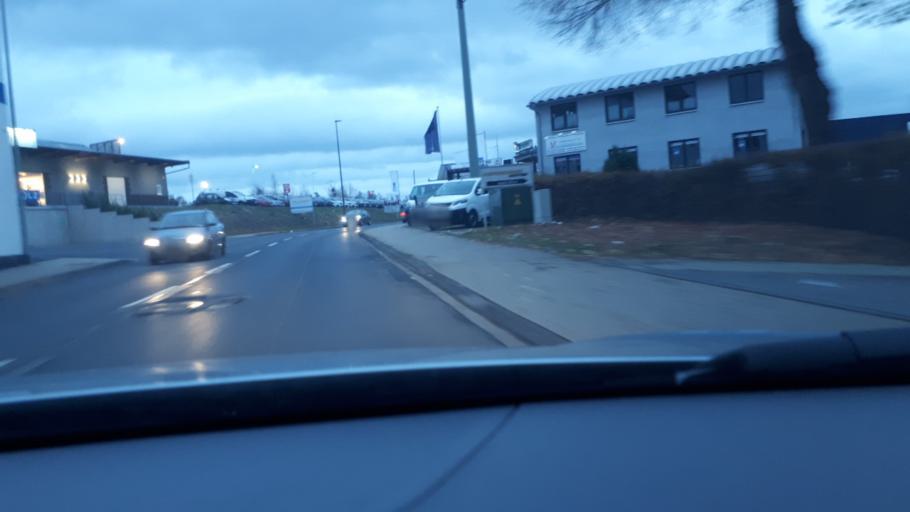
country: DE
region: Rheinland-Pfalz
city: Mayen
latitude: 50.3282
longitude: 7.2400
